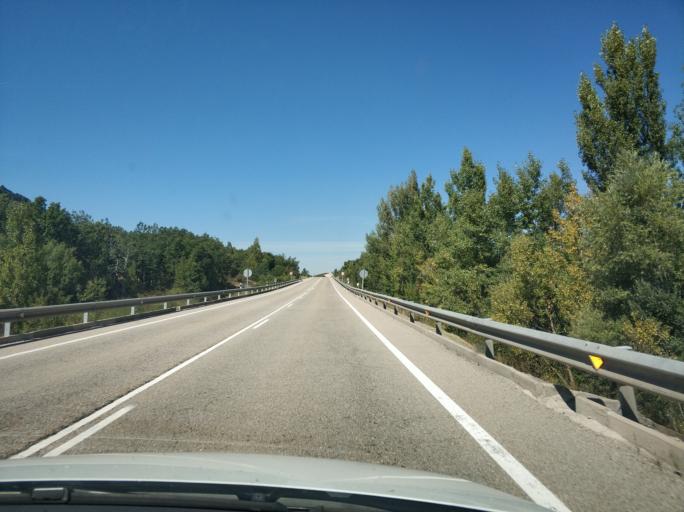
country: ES
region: Castille and Leon
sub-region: Provincia de Burgos
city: Mambrillas de Lara
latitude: 42.0939
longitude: -3.4836
